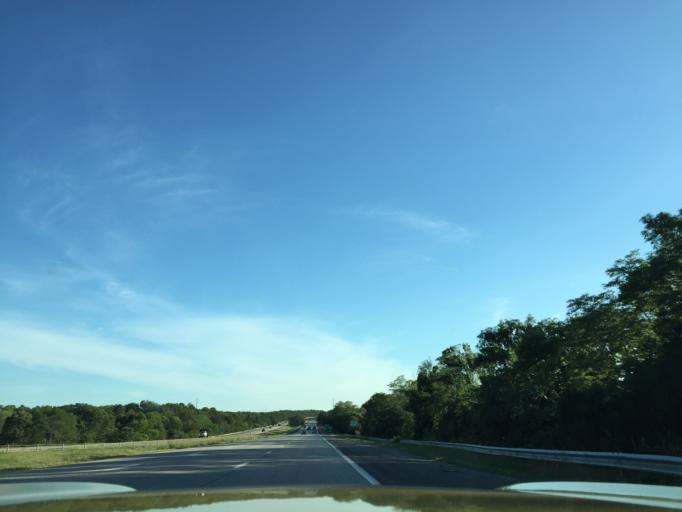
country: US
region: New York
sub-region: Suffolk County
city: Calverton
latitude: 40.9089
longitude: -72.7374
